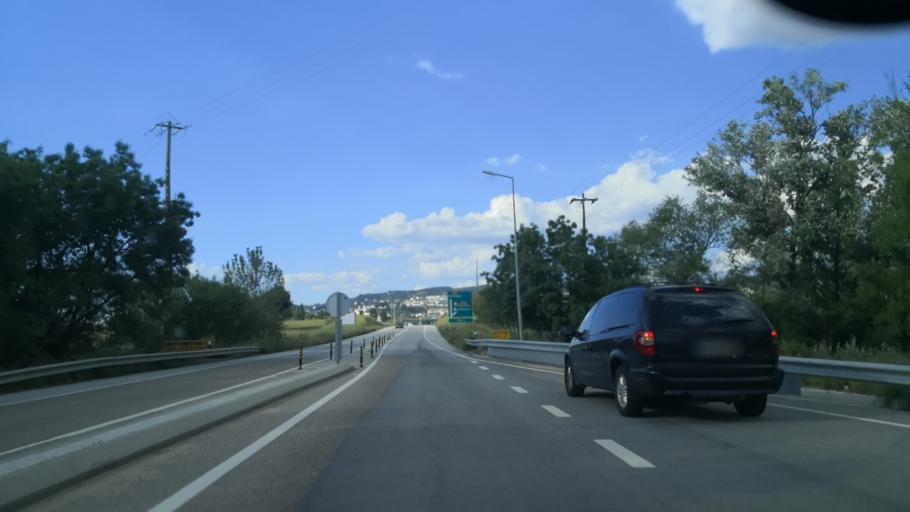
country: PT
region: Portalegre
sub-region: Portalegre
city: Portalegre
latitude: 39.2635
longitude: -7.4438
